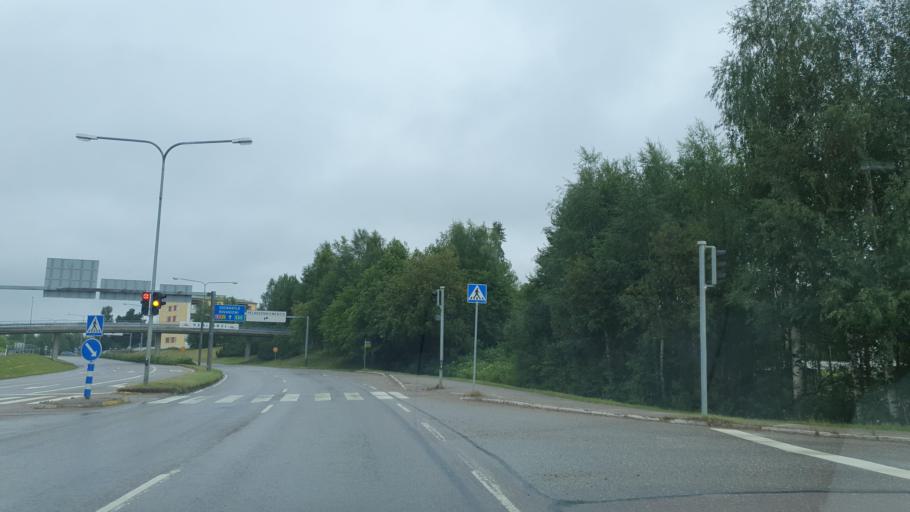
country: FI
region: Lapland
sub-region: Itae-Lappi
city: Kemijaervi
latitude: 66.7211
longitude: 27.4021
